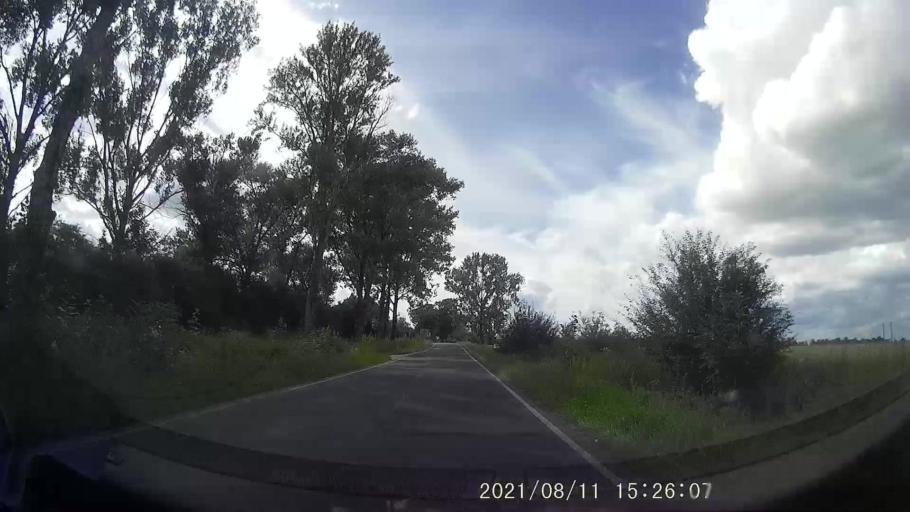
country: PL
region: Lower Silesian Voivodeship
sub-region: Powiat klodzki
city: Bystrzyca Klodzka
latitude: 50.2912
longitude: 16.6654
